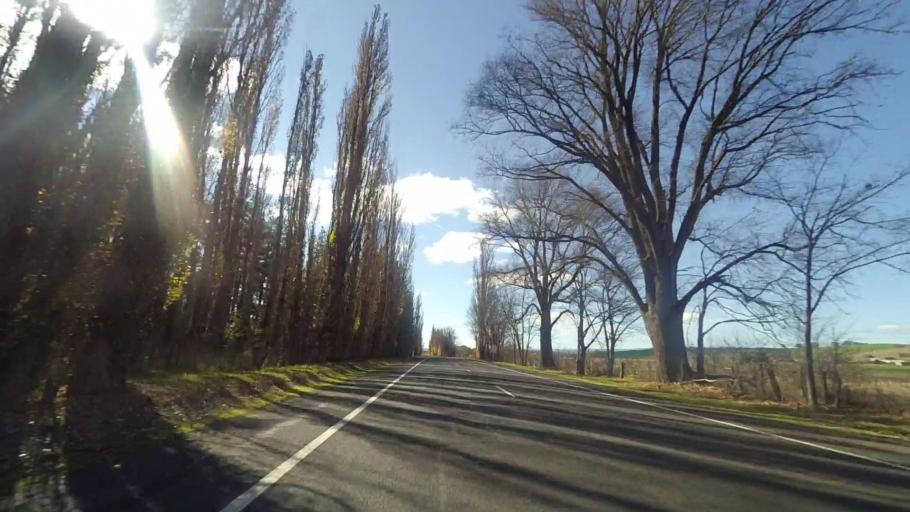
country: AU
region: New South Wales
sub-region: Bathurst Regional
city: Perthville
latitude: -33.4634
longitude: 149.5712
